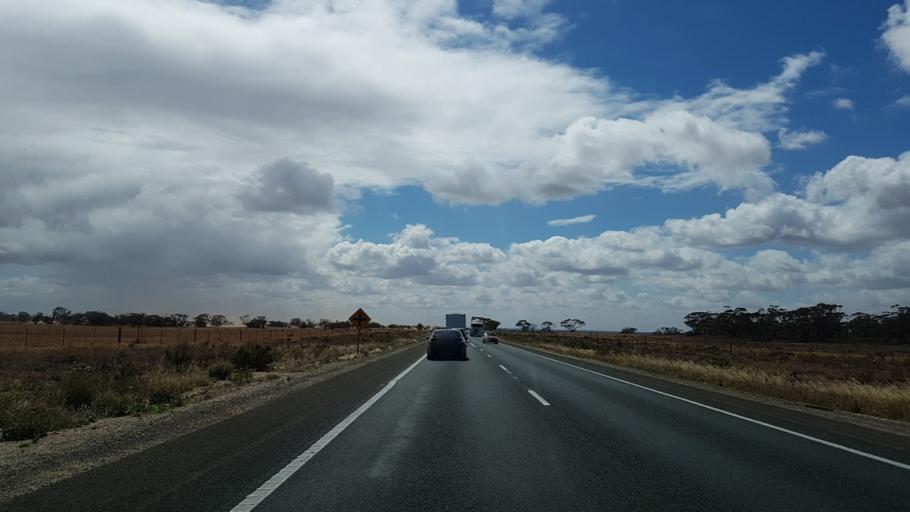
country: AU
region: South Australia
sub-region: Barossa
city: Angaston
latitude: -34.3953
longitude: 139.2990
